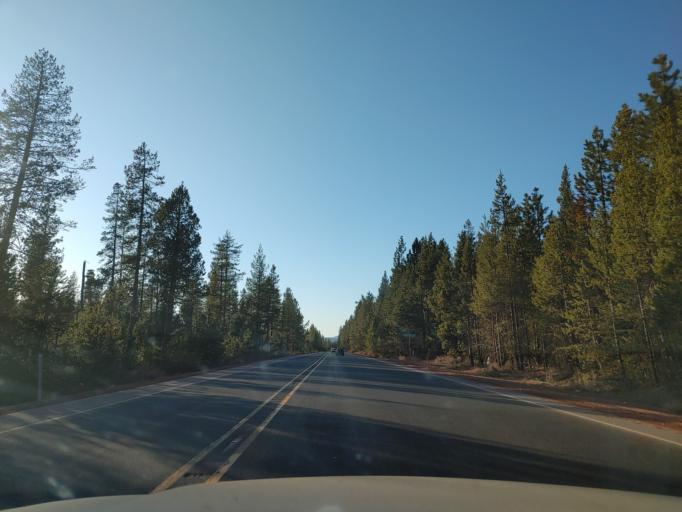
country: US
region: Oregon
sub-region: Deschutes County
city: La Pine
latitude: 43.4570
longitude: -121.8776
